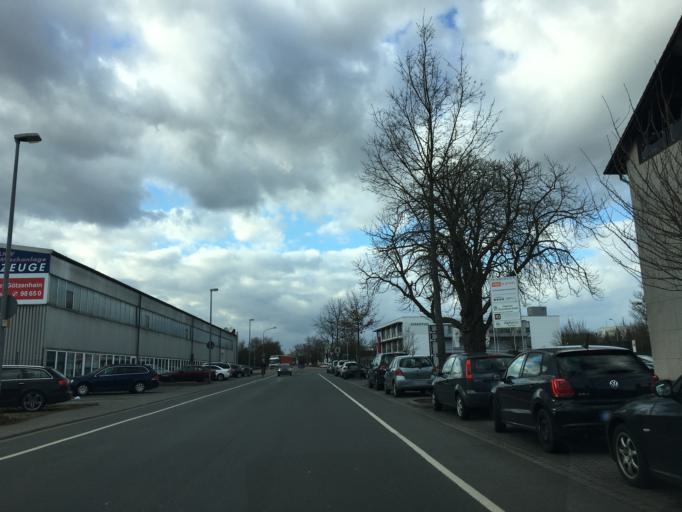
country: DE
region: Hesse
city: Langen
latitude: 50.0015
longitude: 8.6564
